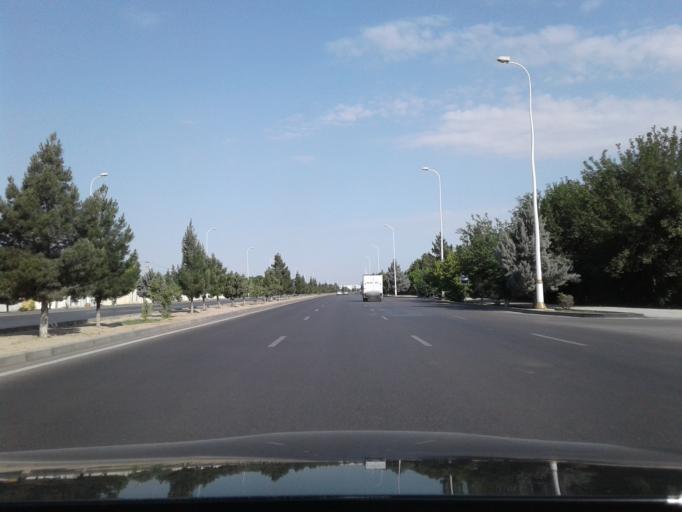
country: TM
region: Ahal
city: Abadan
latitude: 38.0278
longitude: 58.2365
